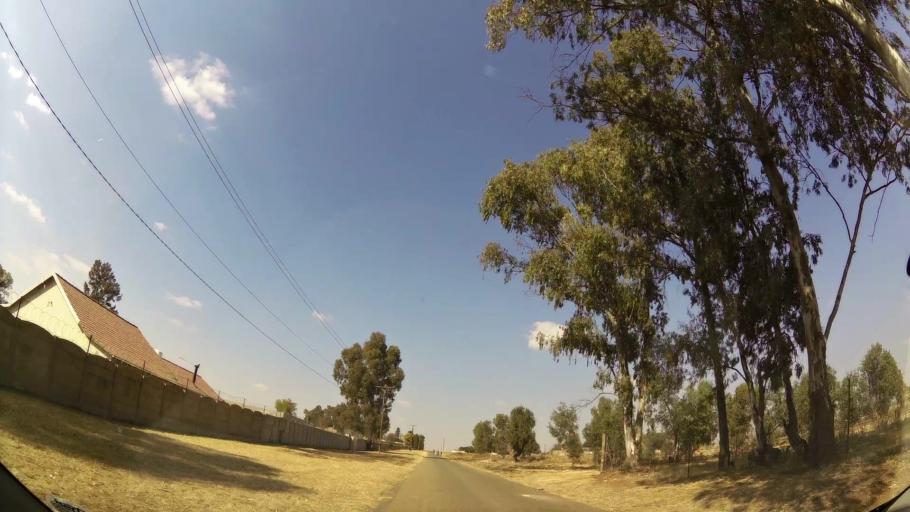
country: ZA
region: Gauteng
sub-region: Ekurhuleni Metropolitan Municipality
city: Benoni
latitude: -26.1151
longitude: 28.4045
